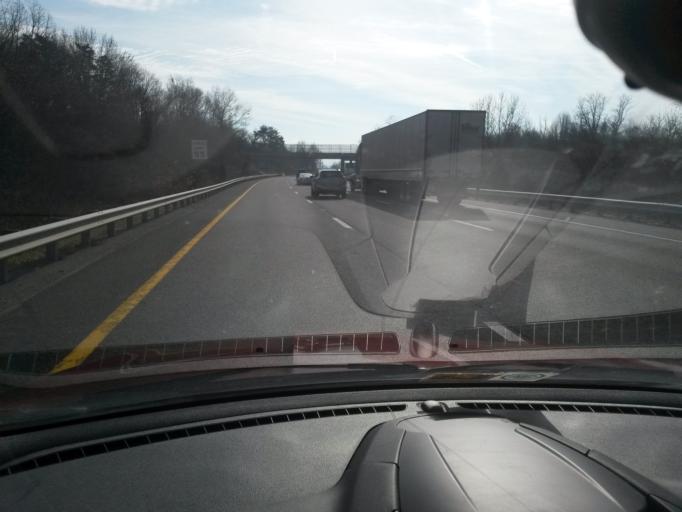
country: US
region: Virginia
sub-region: Roanoke County
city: Hollins
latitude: 37.3374
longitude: -79.9964
